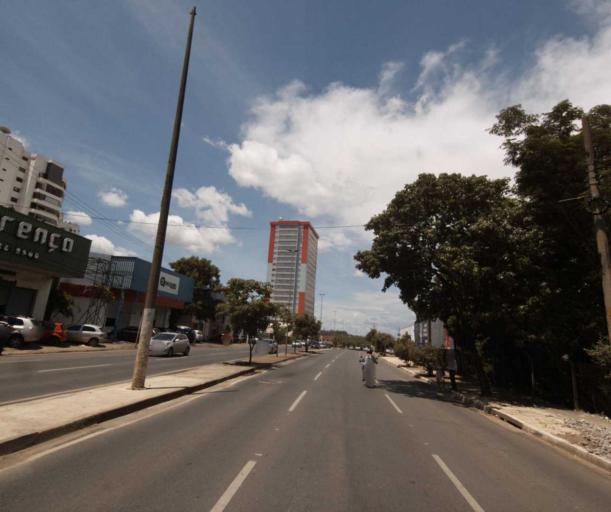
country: BR
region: Mato Grosso
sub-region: Cuiaba
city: Cuiaba
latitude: -15.5810
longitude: -56.1107
